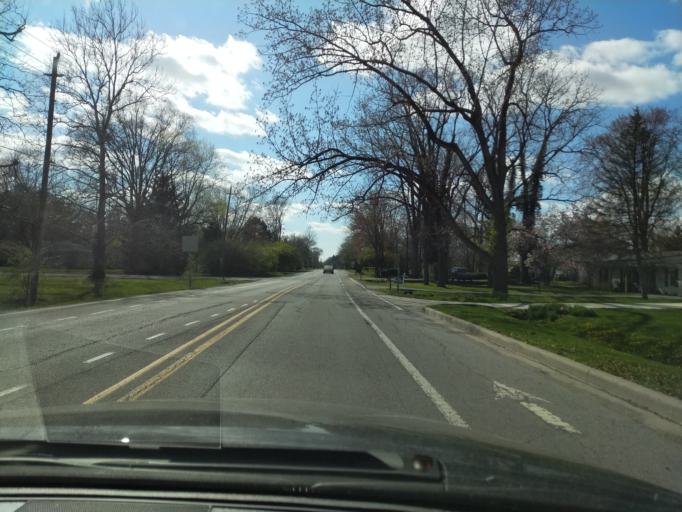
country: US
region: Indiana
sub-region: Marion County
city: Meridian Hills
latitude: 39.8867
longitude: -86.1663
